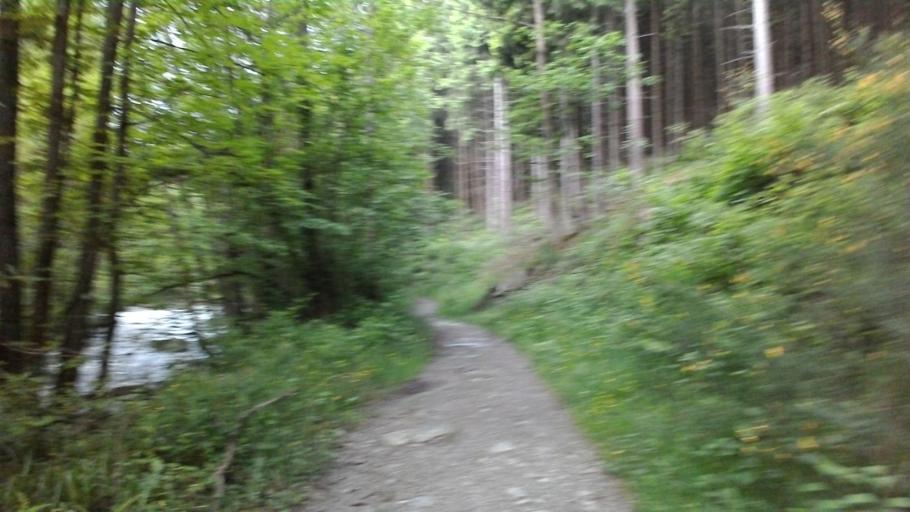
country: DE
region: North Rhine-Westphalia
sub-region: Regierungsbezirk Koln
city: Monschau
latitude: 50.5513
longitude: 6.2121
